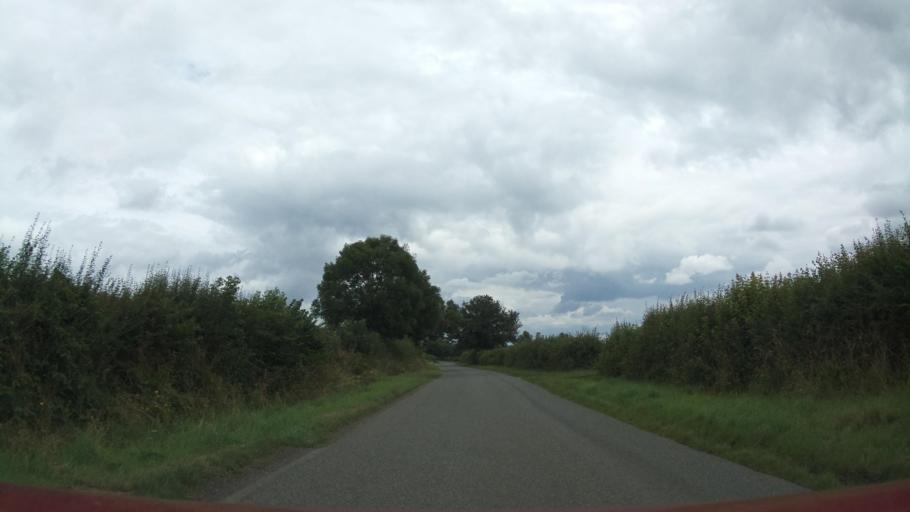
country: GB
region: England
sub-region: District of Rutland
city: Seaton
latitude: 52.5241
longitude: -0.6211
